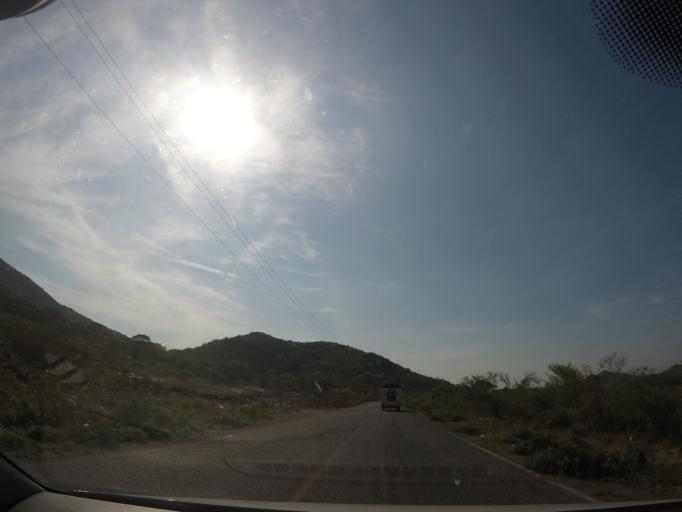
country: MX
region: Oaxaca
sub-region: Salina Cruz
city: Salina Cruz
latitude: 16.2319
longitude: -95.1465
